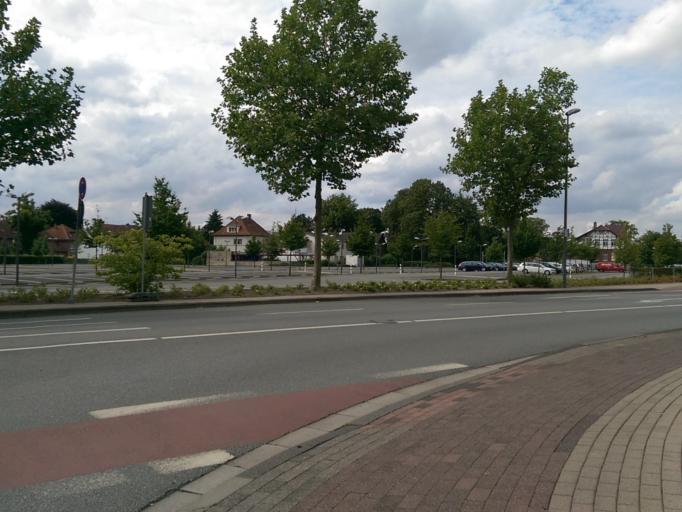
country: DE
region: North Rhine-Westphalia
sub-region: Regierungsbezirk Detmold
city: Guetersloh
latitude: 51.9108
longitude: 8.3967
